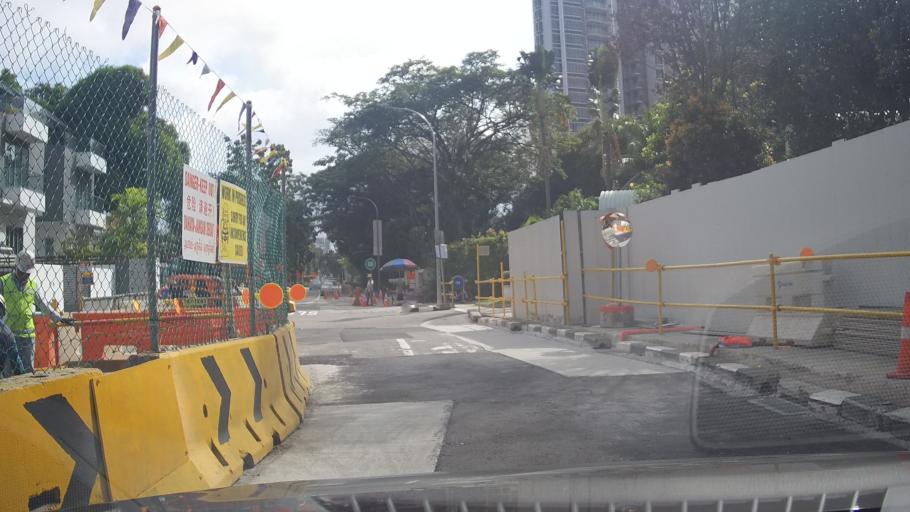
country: SG
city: Singapore
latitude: 1.2970
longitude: 103.8911
